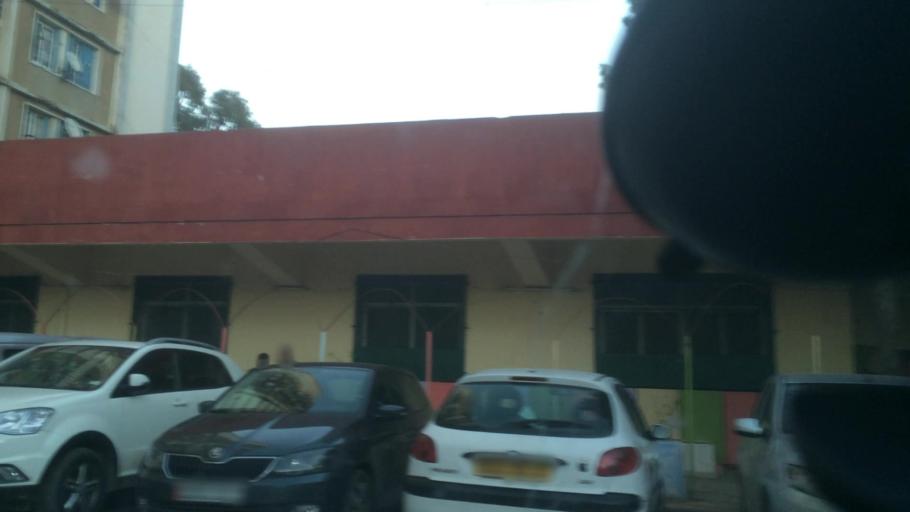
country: DZ
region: Alger
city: Bab Ezzouar
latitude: 36.7261
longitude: 3.1278
